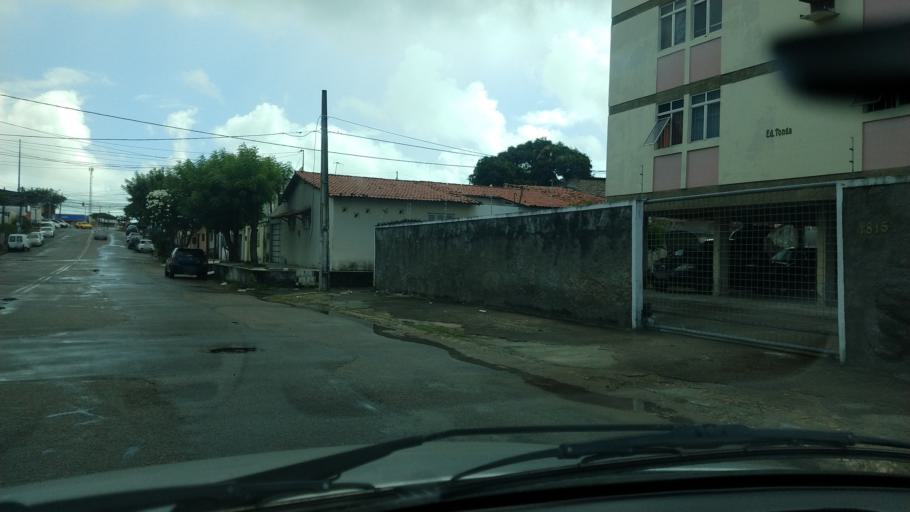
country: BR
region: Rio Grande do Norte
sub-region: Natal
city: Natal
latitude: -5.8100
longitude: -35.2182
